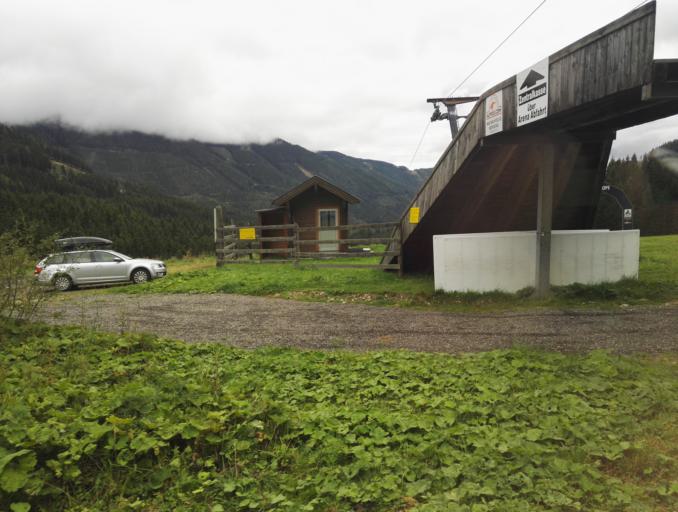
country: AT
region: Styria
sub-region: Politischer Bezirk Leoben
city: Eisenerz
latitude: 47.5194
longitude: 14.9518
